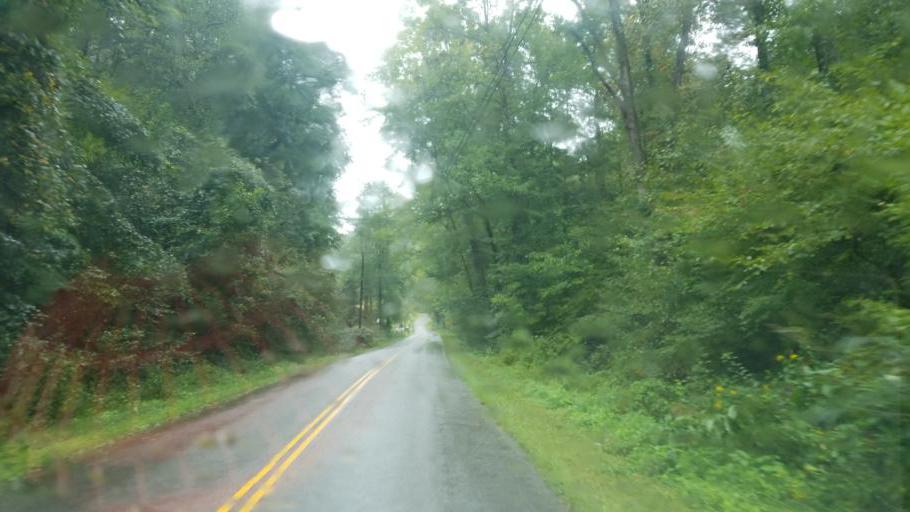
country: US
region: Ohio
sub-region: Scioto County
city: West Portsmouth
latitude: 38.7575
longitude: -83.1040
